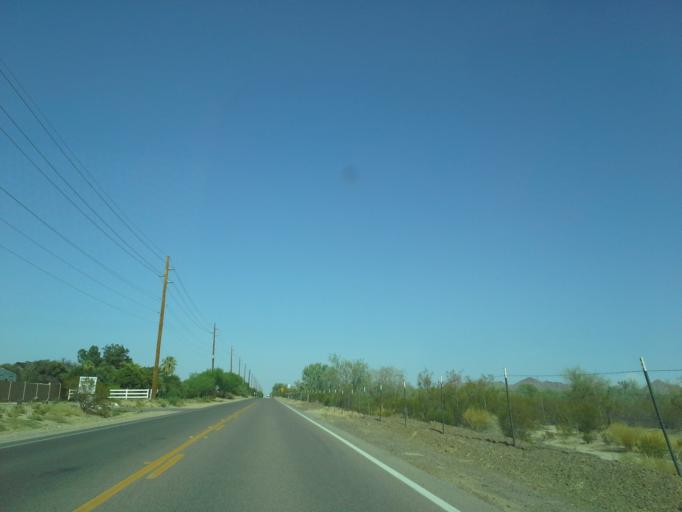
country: US
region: Arizona
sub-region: Maricopa County
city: Queen Creek
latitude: 33.2046
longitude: -111.7031
